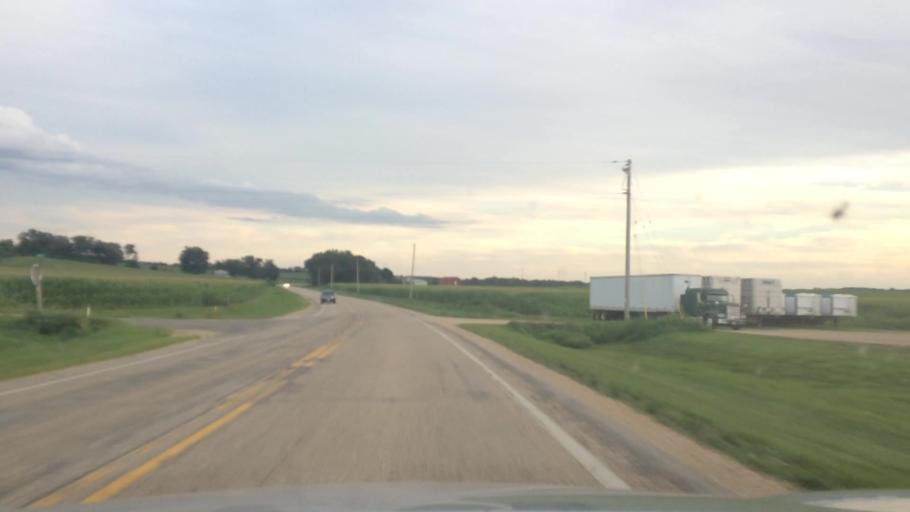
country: US
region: Wisconsin
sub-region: Columbia County
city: Lodi
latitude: 43.2215
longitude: -89.5460
